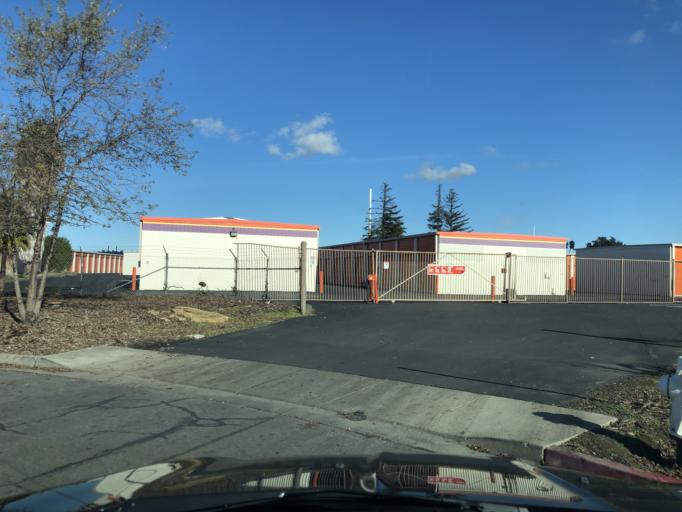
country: US
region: California
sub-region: Contra Costa County
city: Pacheco
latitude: 37.9903
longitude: -122.0695
